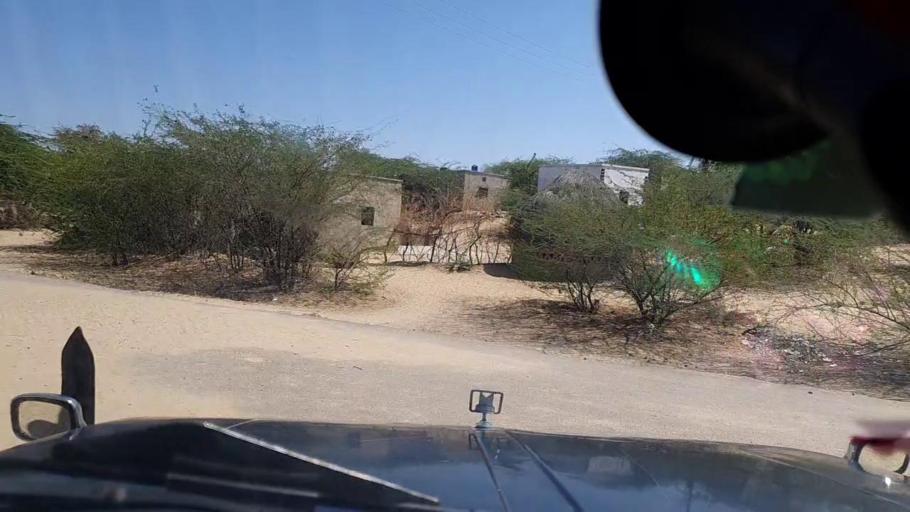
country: PK
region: Sindh
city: Diplo
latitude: 24.5662
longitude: 69.6796
